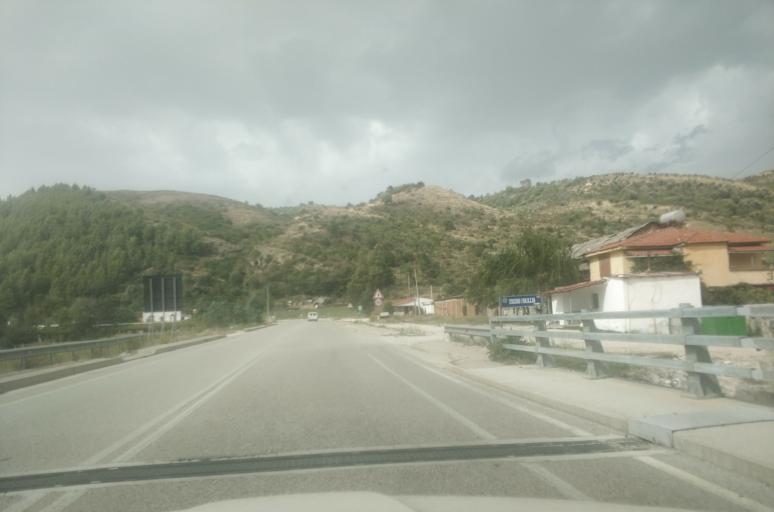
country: AL
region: Gjirokaster
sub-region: Rrethi i Tepelenes
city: Memaliaj
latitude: 40.3518
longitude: 19.9727
